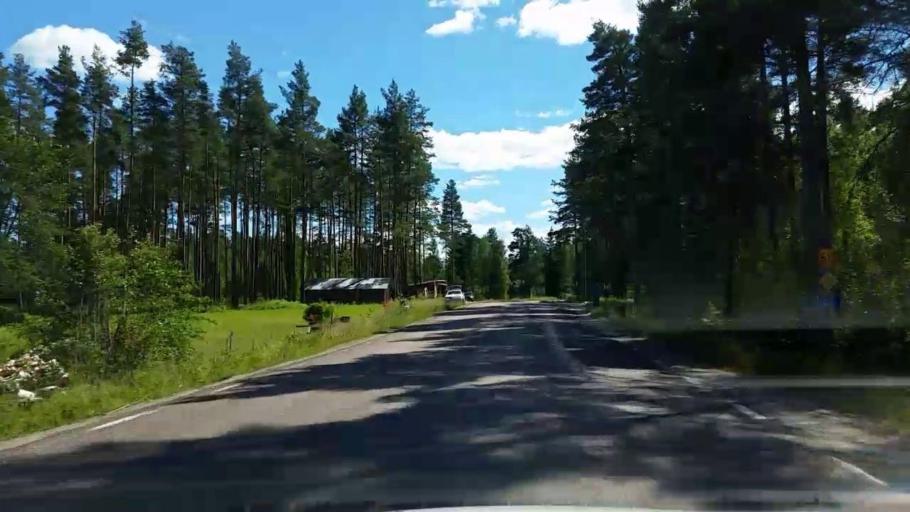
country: SE
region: Dalarna
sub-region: Faluns Kommun
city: Svardsjo
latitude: 60.9855
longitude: 15.7098
